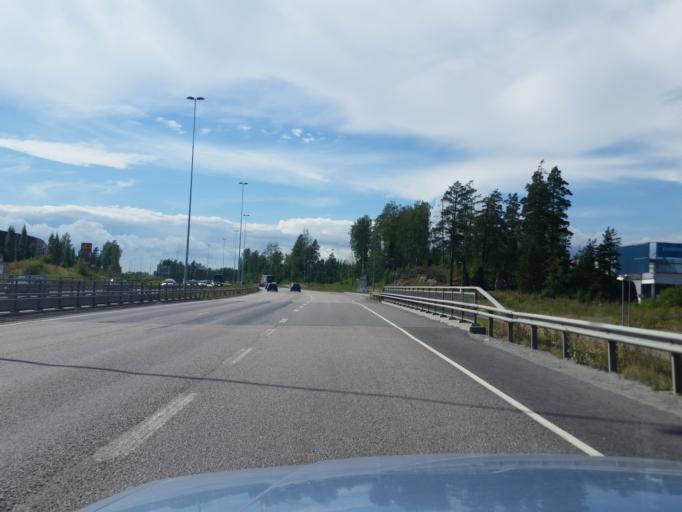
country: FI
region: Uusimaa
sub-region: Helsinki
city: Vantaa
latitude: 60.2969
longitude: 24.9322
